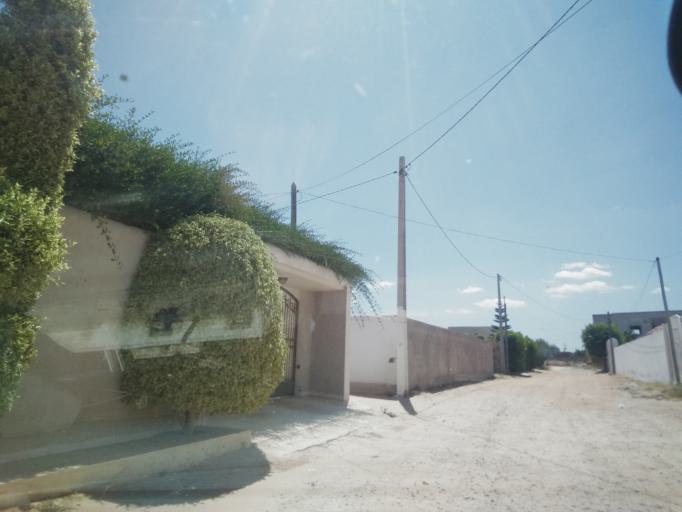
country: TN
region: Safaqis
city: Al Qarmadah
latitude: 34.8229
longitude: 10.7651
